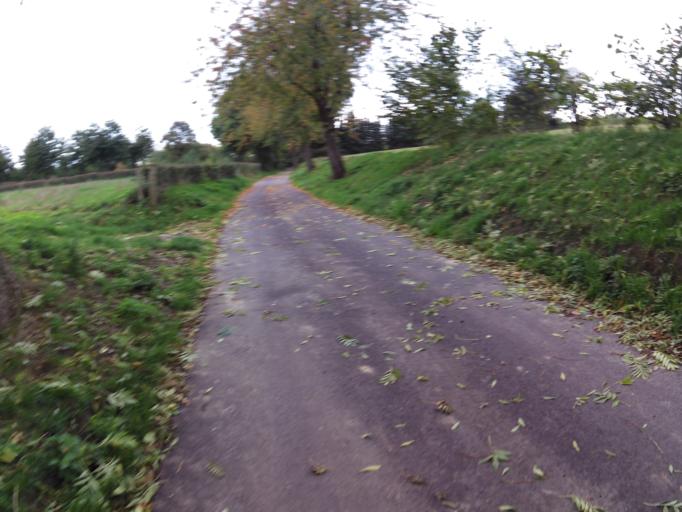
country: NL
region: Limburg
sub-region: Gemeente Voerendaal
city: Ubachsberg
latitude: 50.8596
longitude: 5.9479
